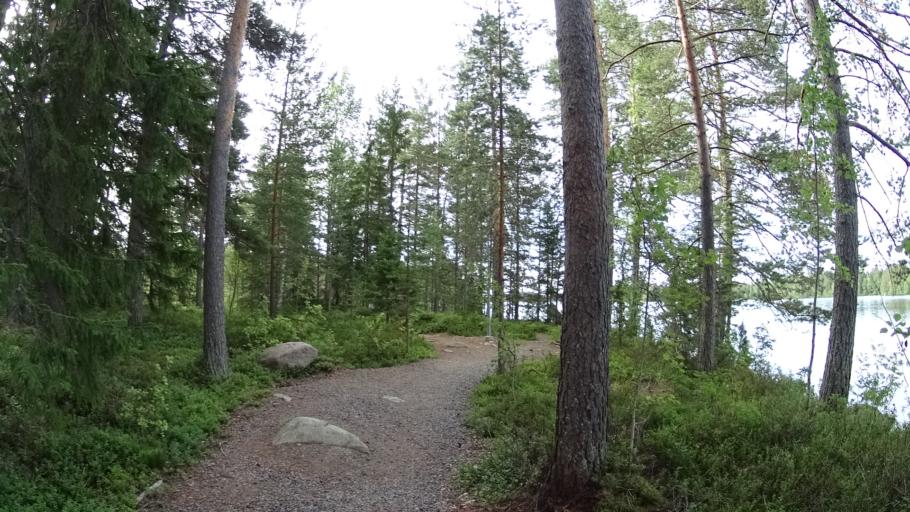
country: FI
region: Southern Ostrobothnia
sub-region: Kuusiokunnat
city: AEhtaeri
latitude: 62.5376
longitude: 24.1760
